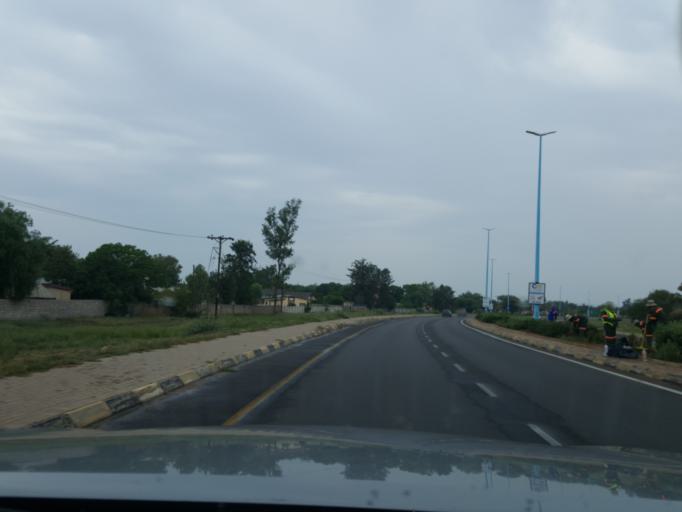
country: BW
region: South East
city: Gaborone
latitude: -24.6173
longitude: 25.9309
